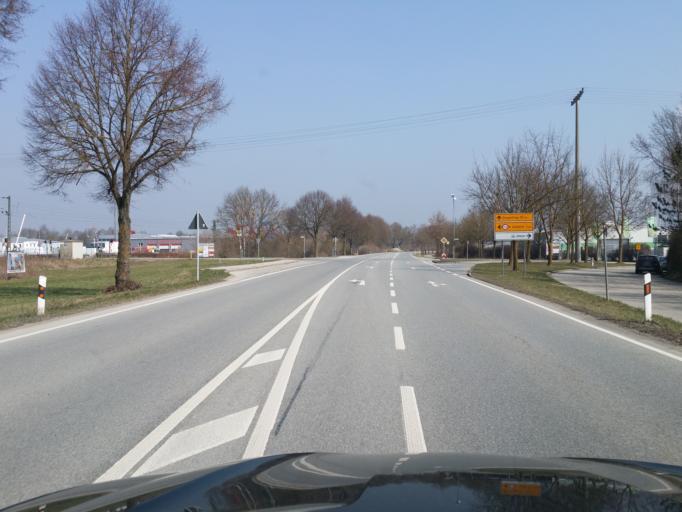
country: DE
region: Bavaria
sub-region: Lower Bavaria
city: Essenbach
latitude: 48.5856
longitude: 12.2029
